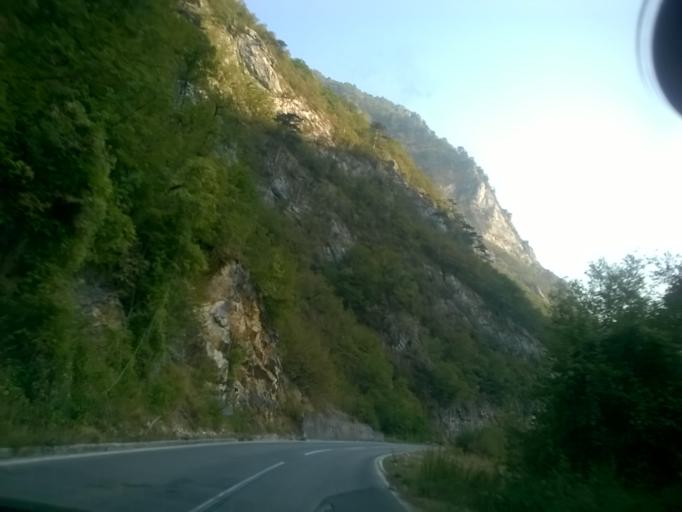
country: ME
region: Opstina Pluzine
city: Pluzine
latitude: 43.2107
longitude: 18.8591
